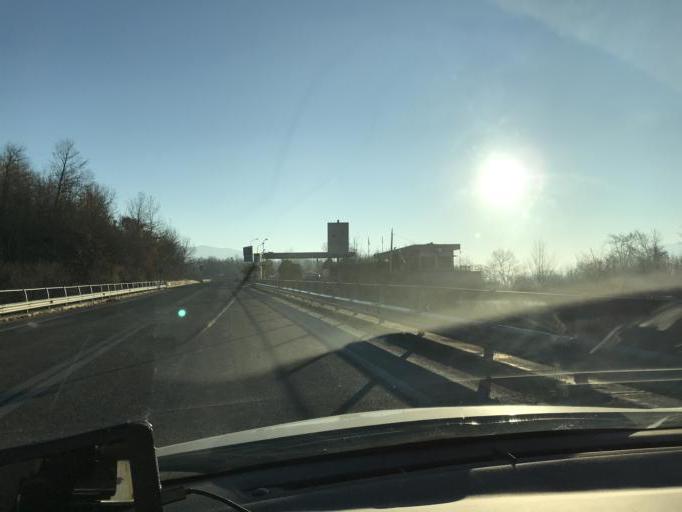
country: IT
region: Latium
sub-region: Provincia di Rieti
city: Fiamignano
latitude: 42.2618
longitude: 13.0913
